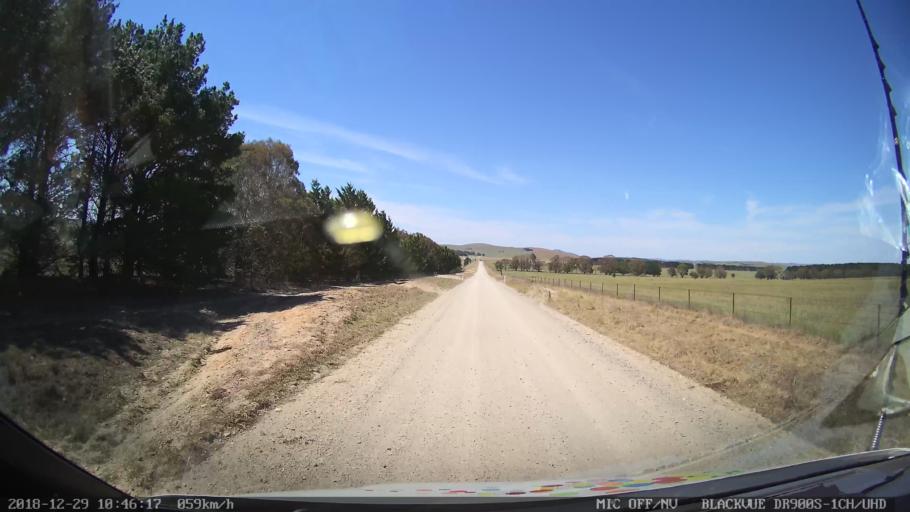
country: AU
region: New South Wales
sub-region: Palerang
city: Bungendore
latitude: -35.0489
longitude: 149.5166
